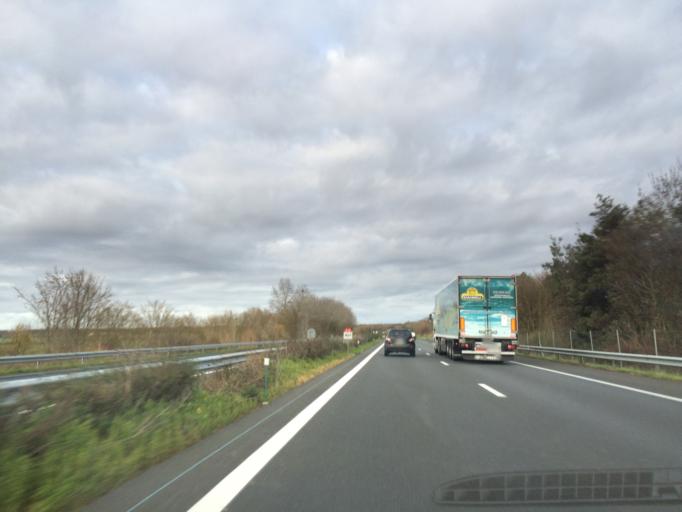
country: FR
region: Poitou-Charentes
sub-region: Departement de la Charente-Maritime
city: Saint-Jean-d'Angely
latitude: 46.0680
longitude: -0.5336
